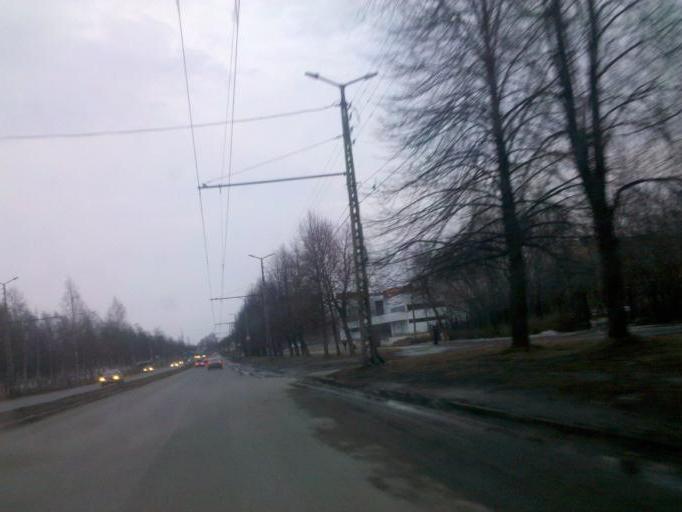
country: RU
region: Republic of Karelia
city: Petrozavodsk
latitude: 61.8050
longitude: 34.3451
